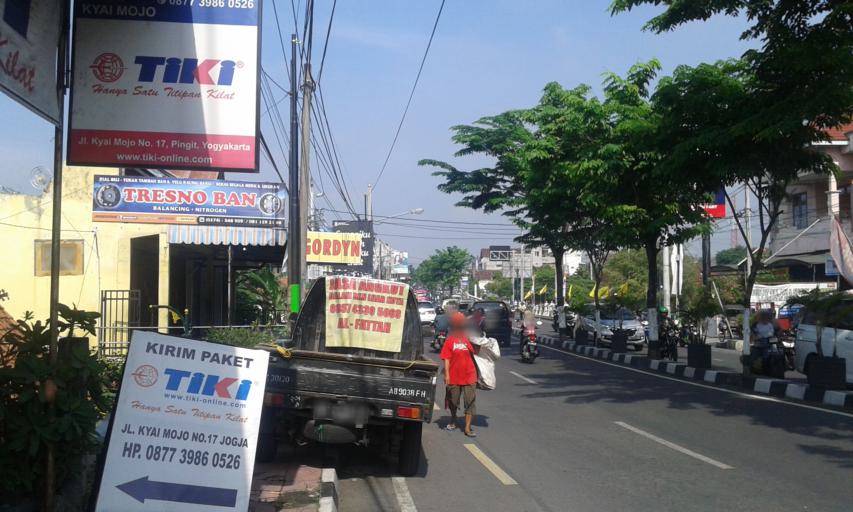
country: ID
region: Daerah Istimewa Yogyakarta
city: Yogyakarta
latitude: -7.7829
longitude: 110.3576
